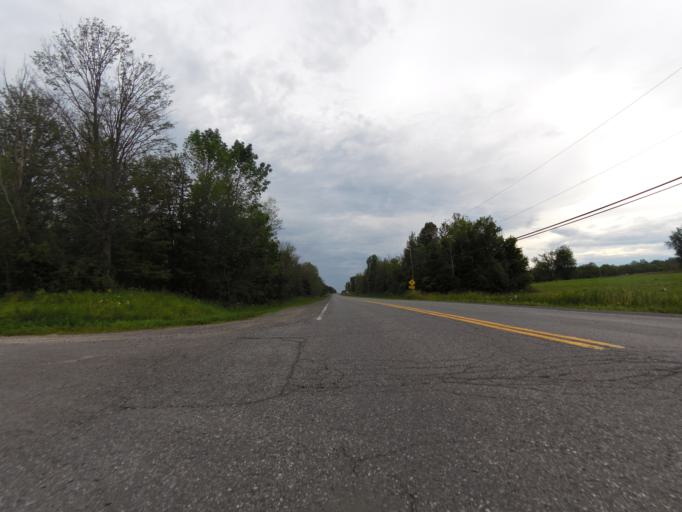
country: CA
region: Ontario
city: Carleton Place
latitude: 45.1553
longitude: -76.3025
